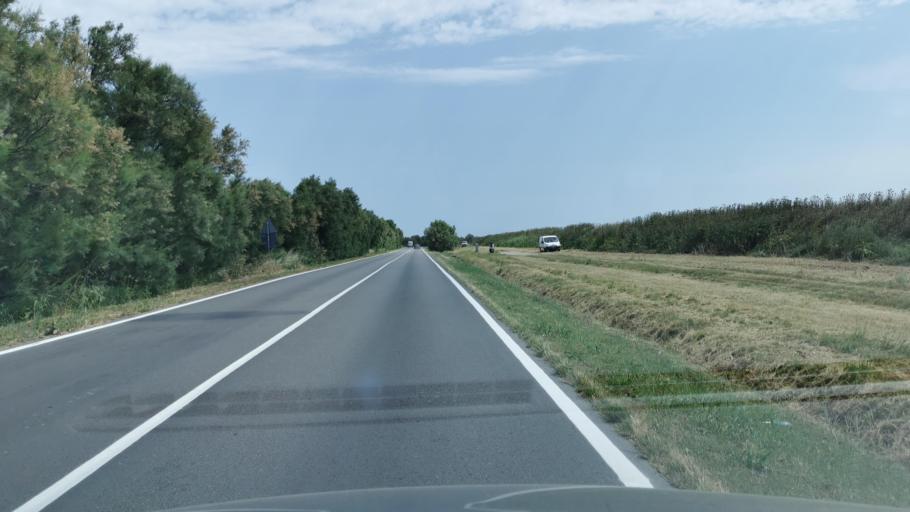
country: IT
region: Emilia-Romagna
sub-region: Provincia di Ferrara
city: Comacchio
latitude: 44.6837
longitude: 12.1970
